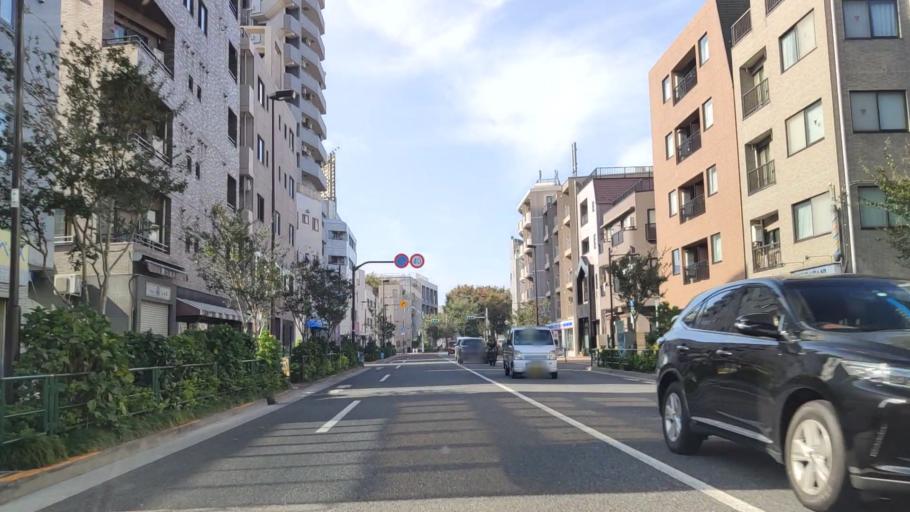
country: JP
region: Tokyo
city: Tokyo
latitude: 35.6869
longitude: 139.6759
